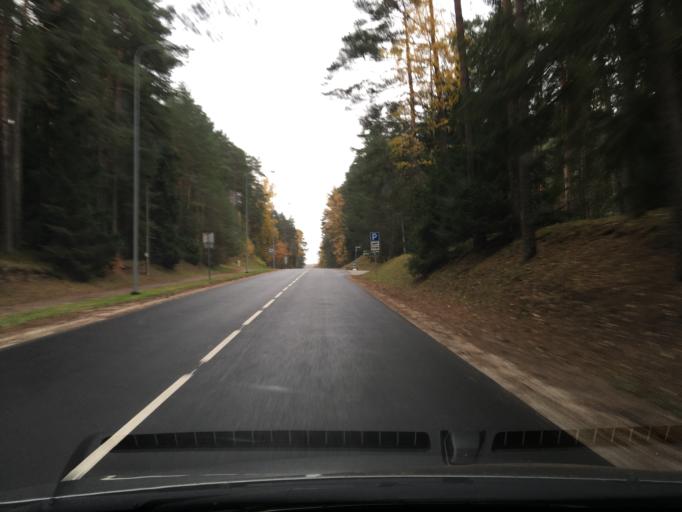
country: EE
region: Tartu
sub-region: Elva linn
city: Elva
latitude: 58.2291
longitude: 26.4073
